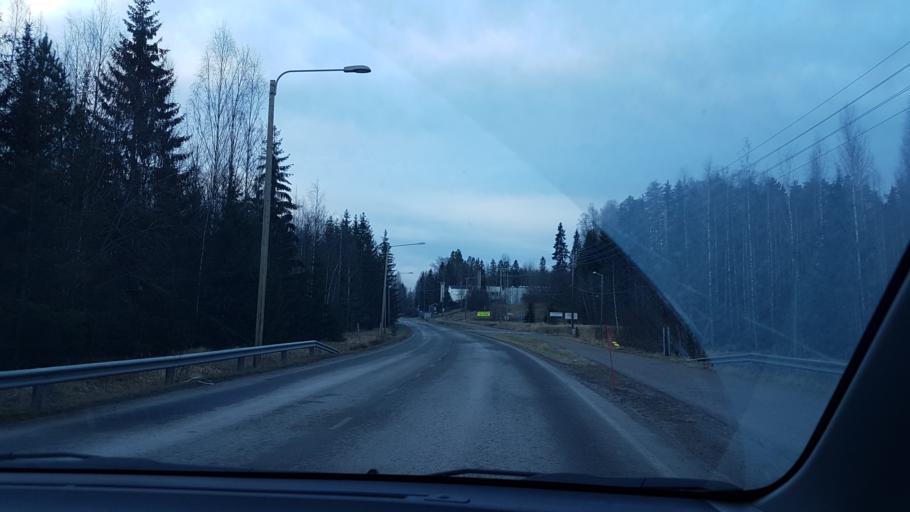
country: FI
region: Uusimaa
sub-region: Helsinki
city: Nurmijaervi
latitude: 60.3611
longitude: 24.7447
